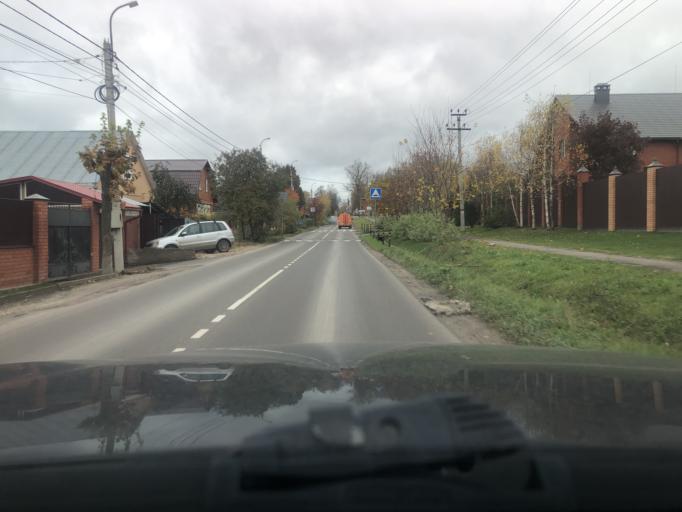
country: RU
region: Moskovskaya
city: Sergiyev Posad
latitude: 56.3039
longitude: 38.1097
